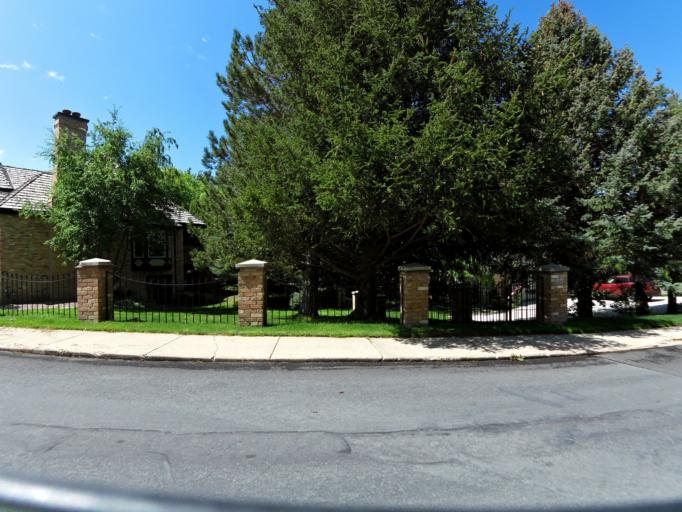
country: US
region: Utah
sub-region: Weber County
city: Uintah
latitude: 41.1777
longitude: -111.9344
